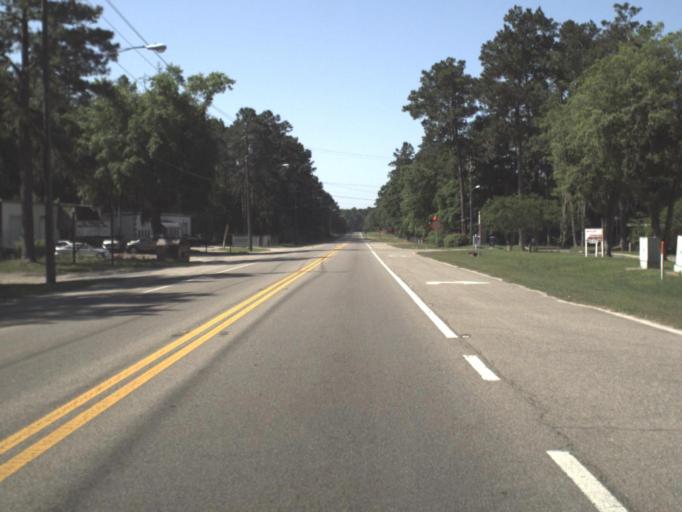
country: US
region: Florida
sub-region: Leon County
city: Tallahassee
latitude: 30.4517
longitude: -84.3458
